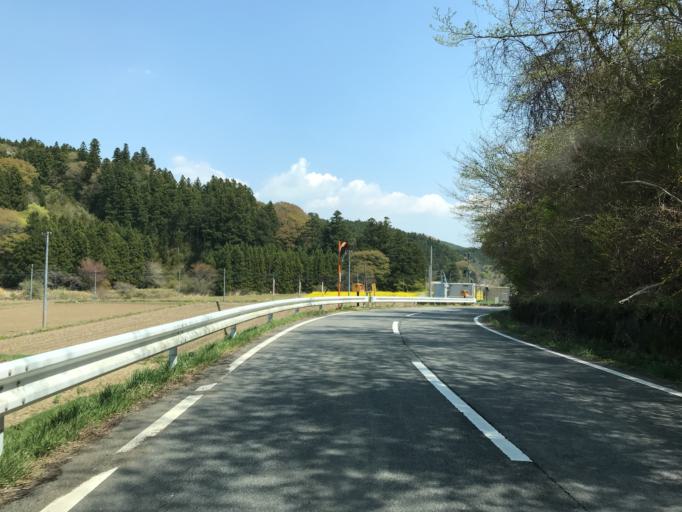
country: JP
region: Ibaraki
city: Kitaibaraki
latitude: 36.9685
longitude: 140.6522
